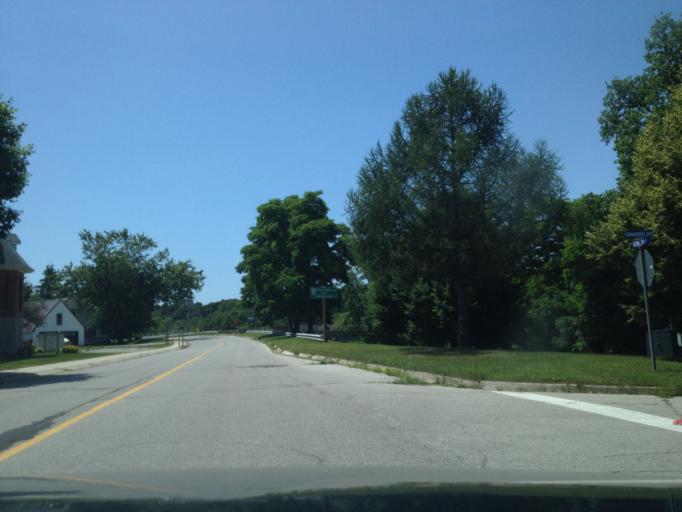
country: CA
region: Ontario
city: Aylmer
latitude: 42.6490
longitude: -80.8054
